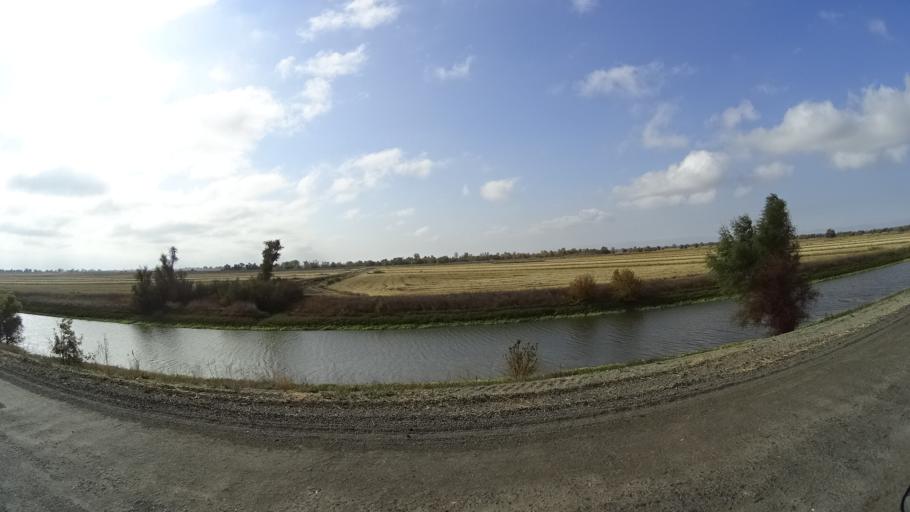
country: US
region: California
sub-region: Yolo County
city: Woodland
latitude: 38.8183
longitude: -121.7864
